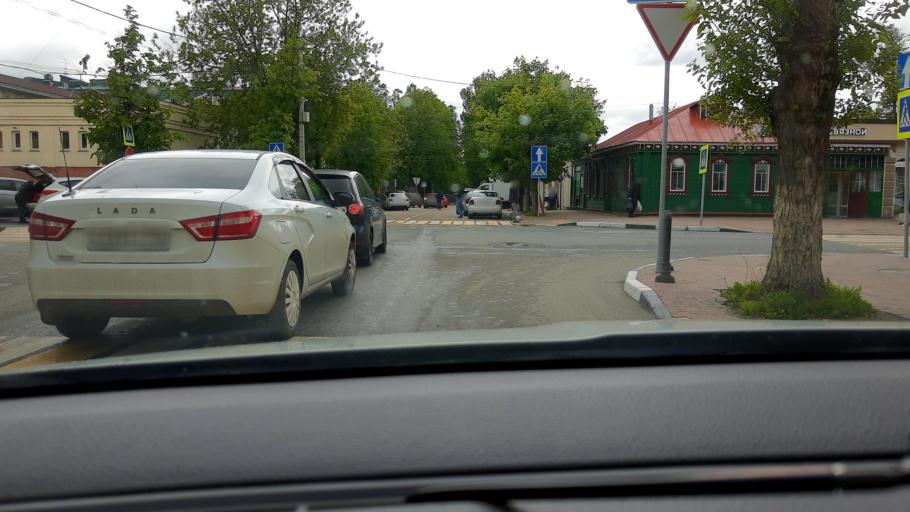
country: RU
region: Moskovskaya
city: Zvenigorod
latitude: 55.7299
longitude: 36.8586
